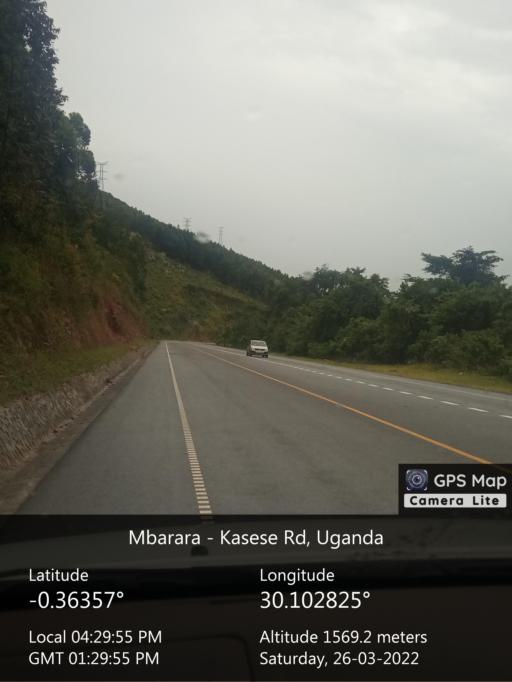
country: UG
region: Western Region
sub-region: Rubirizi District
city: Rubirizi
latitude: -0.3636
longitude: 30.1028
